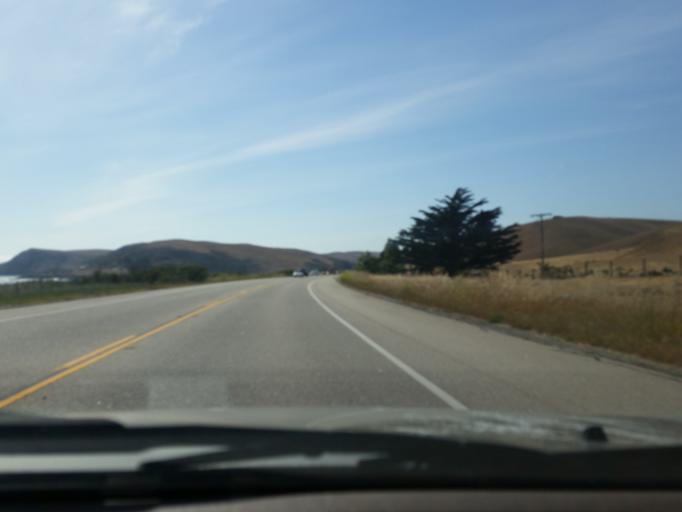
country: US
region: California
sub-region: San Luis Obispo County
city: Cayucos
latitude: 35.4555
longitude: -120.9554
